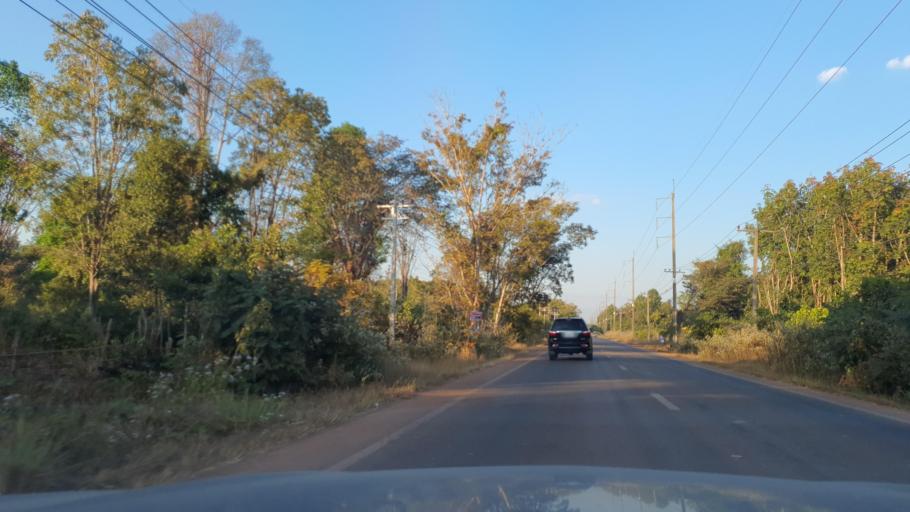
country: TH
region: Nakhon Phanom
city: Si Songkhram
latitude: 17.5982
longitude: 104.2381
